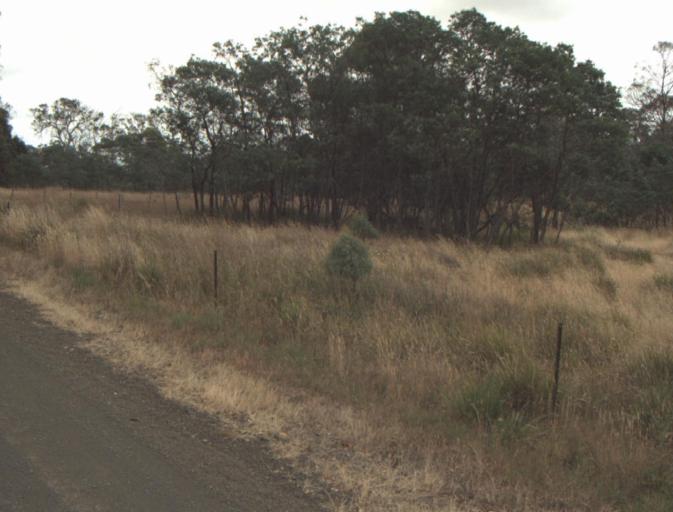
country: AU
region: Tasmania
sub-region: Northern Midlands
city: Evandale
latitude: -41.5268
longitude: 147.3606
